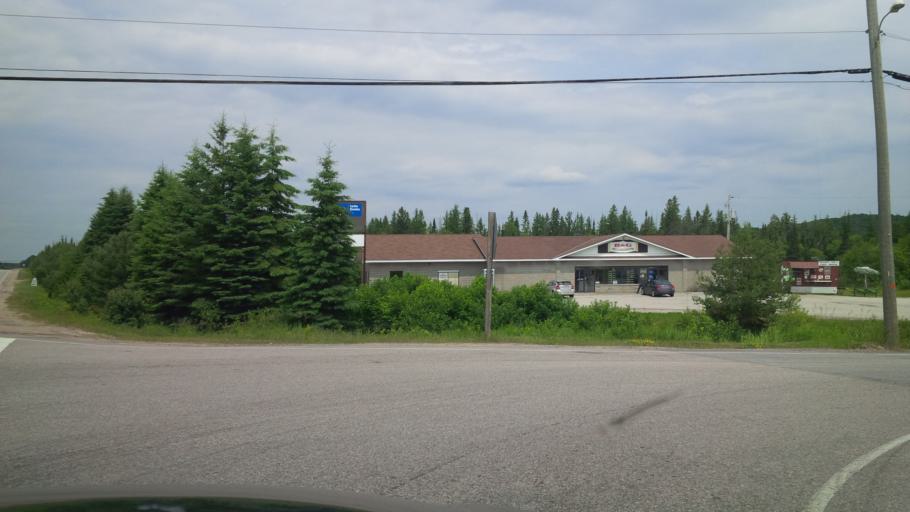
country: CA
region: Ontario
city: Huntsville
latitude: 45.5280
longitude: -79.3205
